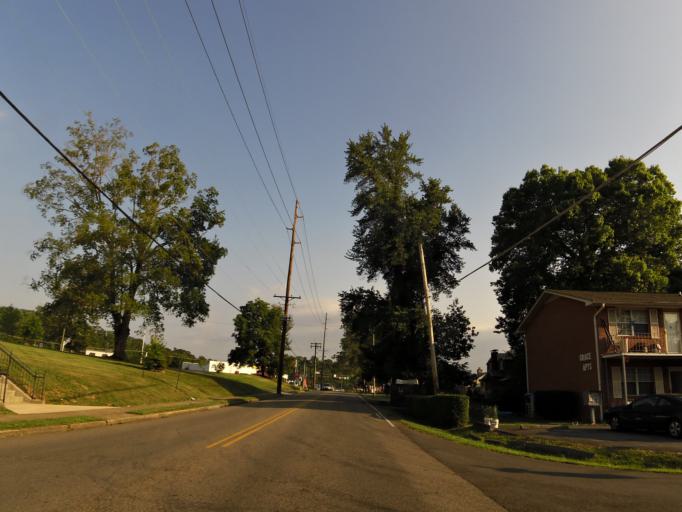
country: US
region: Tennessee
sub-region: Knox County
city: Knoxville
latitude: 36.0296
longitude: -83.9224
